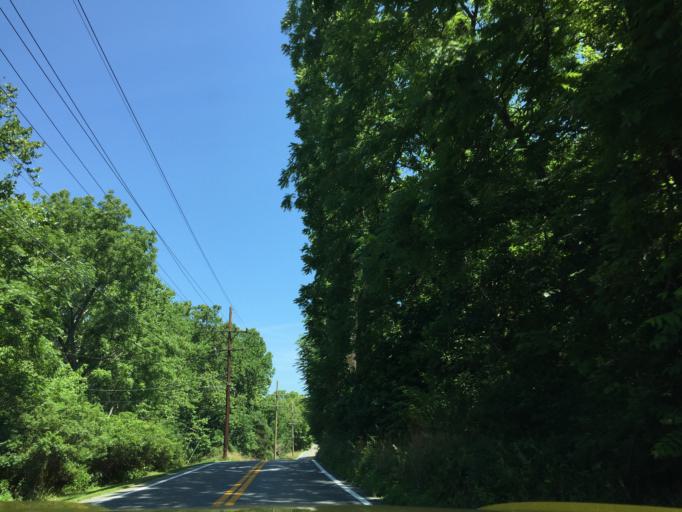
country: US
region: West Virginia
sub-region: Jefferson County
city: Bolivar
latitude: 39.3299
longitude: -77.7640
